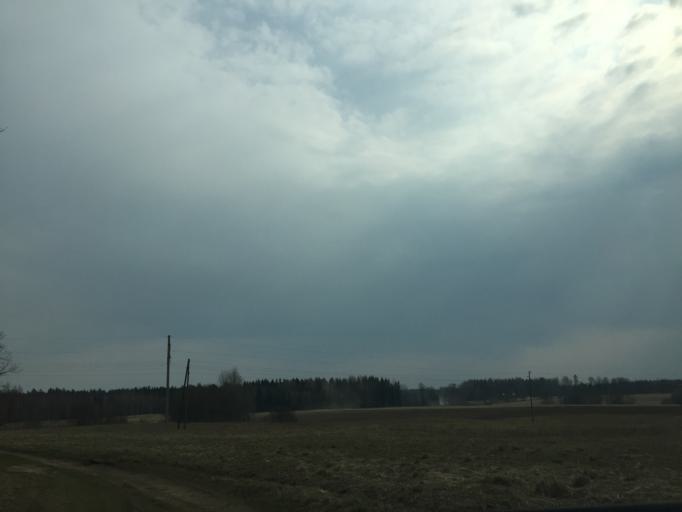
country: LV
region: Amatas Novads
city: Drabesi
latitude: 57.2283
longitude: 25.1945
